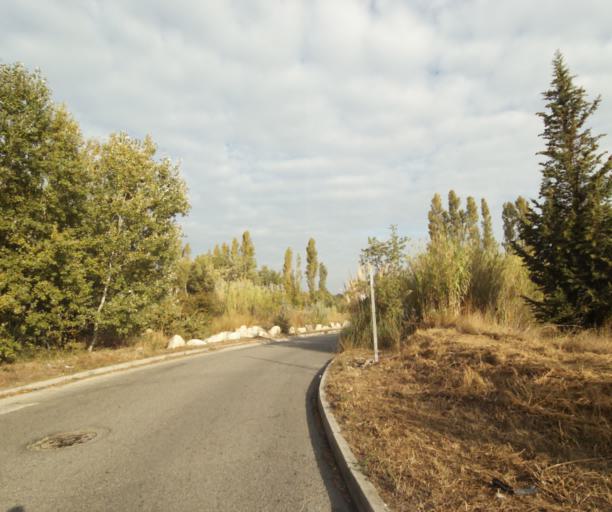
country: FR
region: Provence-Alpes-Cote d'Azur
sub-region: Departement des Bouches-du-Rhone
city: Saint-Victoret
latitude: 43.4207
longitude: 5.2599
